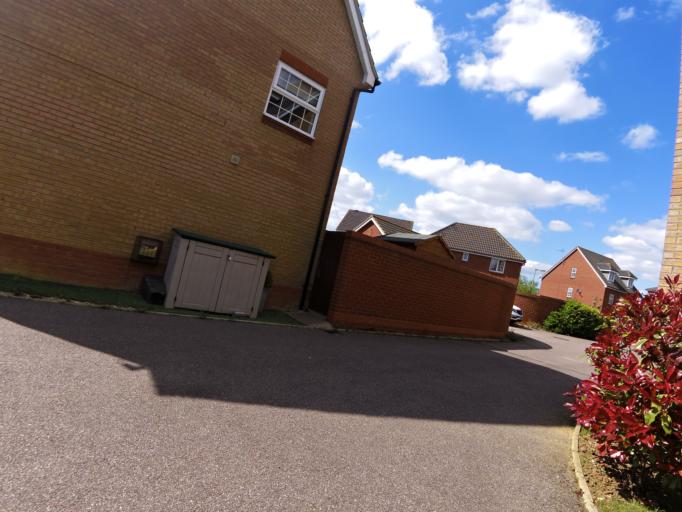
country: GB
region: England
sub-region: Suffolk
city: Kessingland
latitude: 52.4474
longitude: 1.7111
